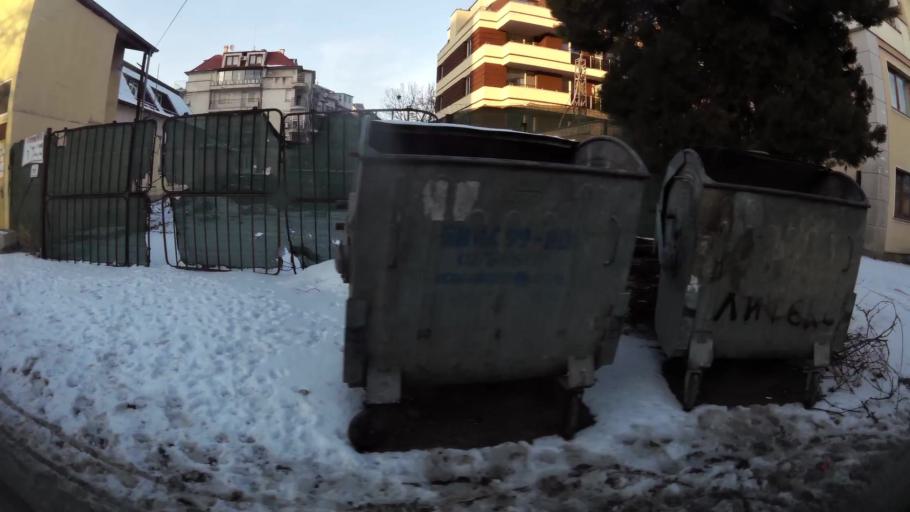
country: BG
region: Sofia-Capital
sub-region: Stolichna Obshtina
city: Sofia
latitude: 42.6933
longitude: 23.3641
